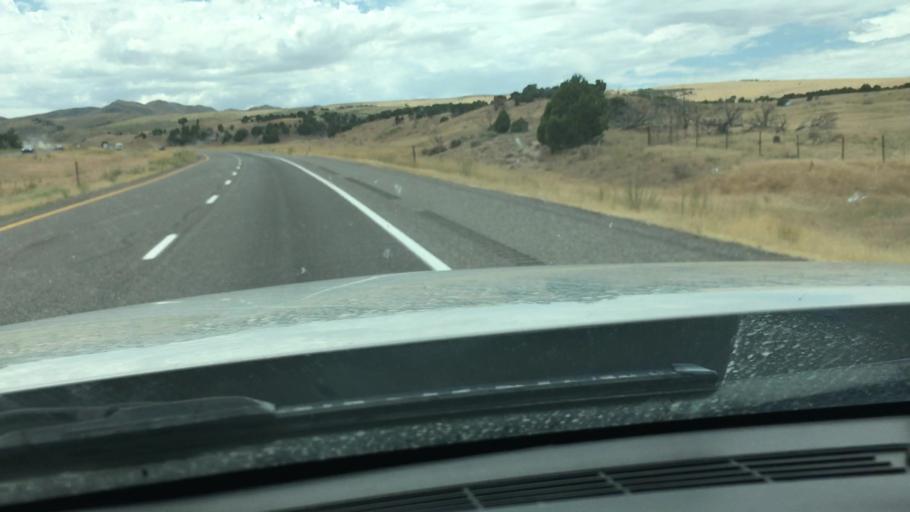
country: US
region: Utah
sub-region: Millard County
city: Fillmore
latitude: 38.7207
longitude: -112.5975
